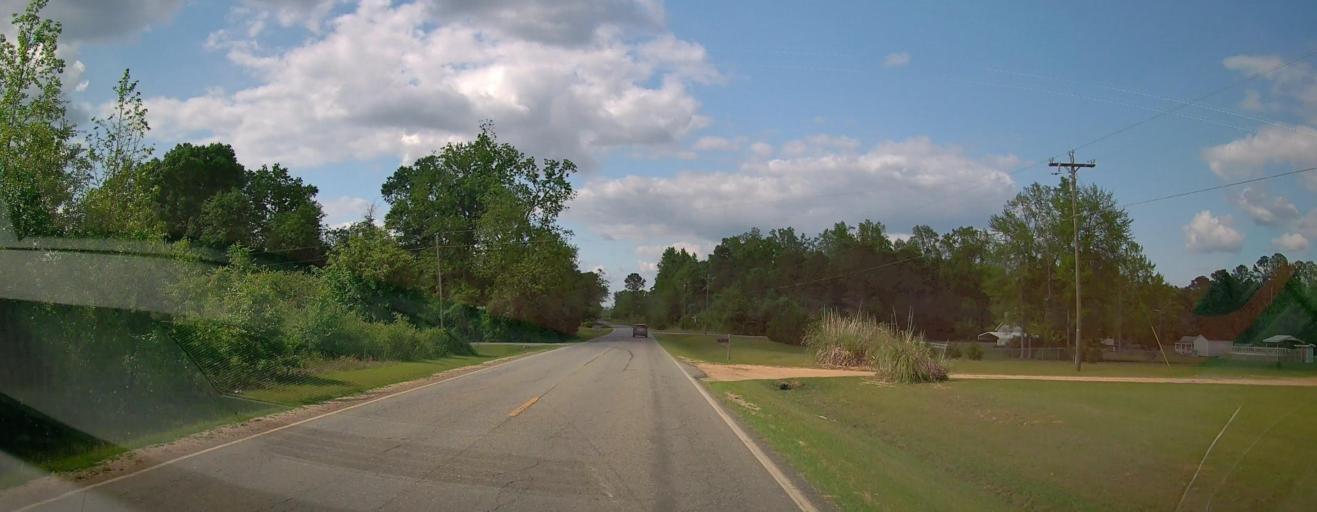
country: US
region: Georgia
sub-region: Laurens County
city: East Dublin
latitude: 32.5944
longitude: -82.8655
